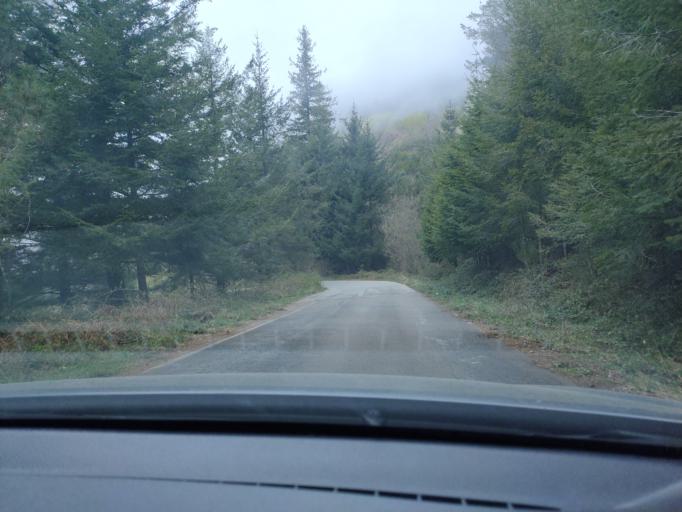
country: ES
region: Catalonia
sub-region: Provincia de Barcelona
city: Fogars de Montclus
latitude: 41.7565
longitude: 2.4560
